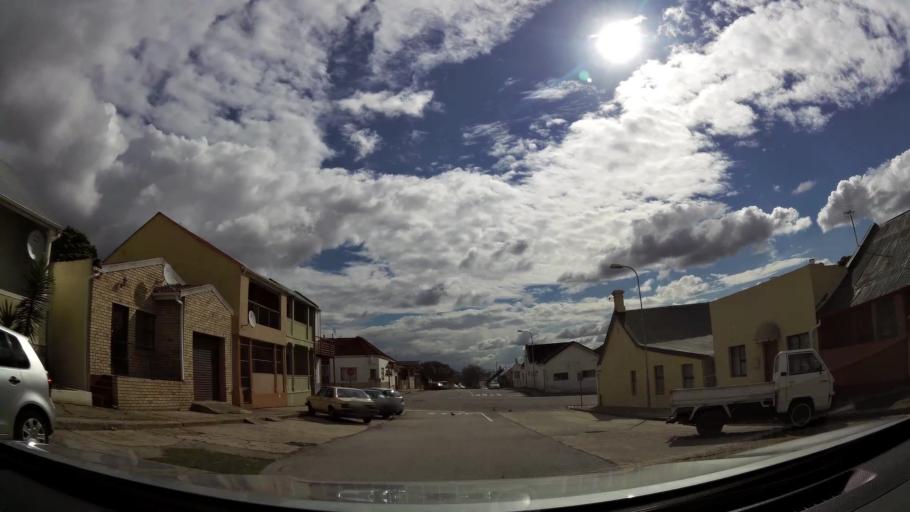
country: ZA
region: Eastern Cape
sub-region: Nelson Mandela Bay Metropolitan Municipality
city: Port Elizabeth
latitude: -33.9542
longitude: 25.6087
